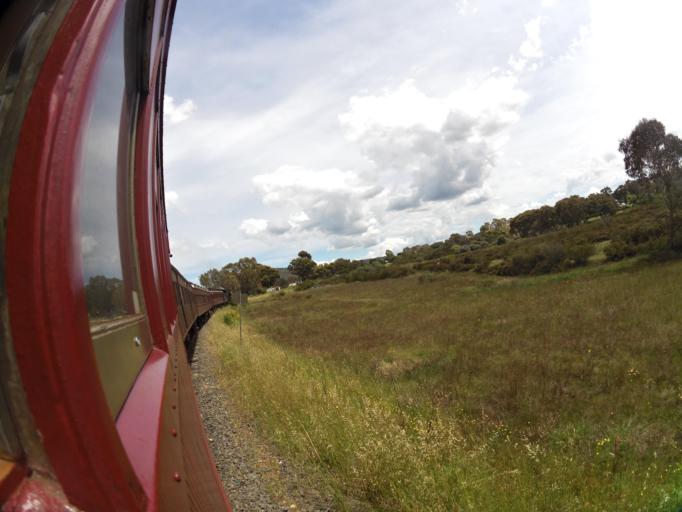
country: AU
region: Victoria
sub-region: Mount Alexander
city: Castlemaine
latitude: -36.9926
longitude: 144.0790
